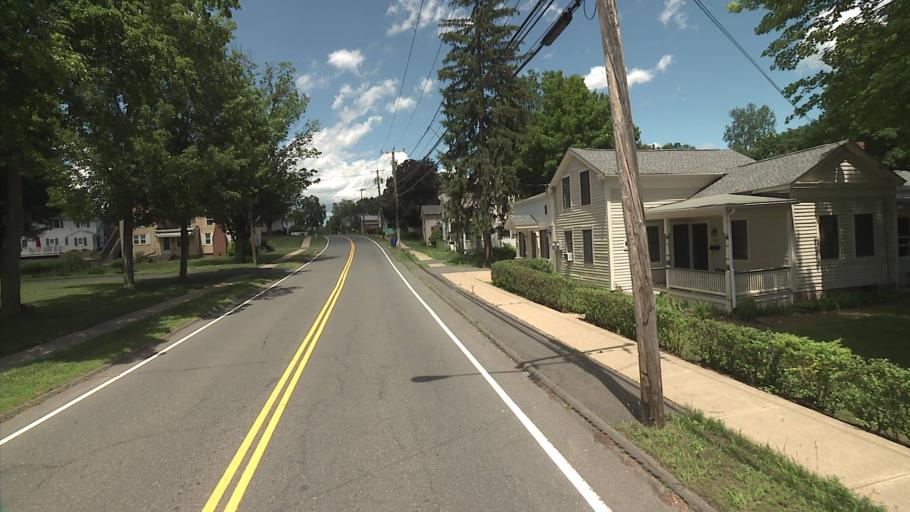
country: US
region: Connecticut
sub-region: Hartford County
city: Hazardville
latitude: 41.9870
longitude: -72.5393
